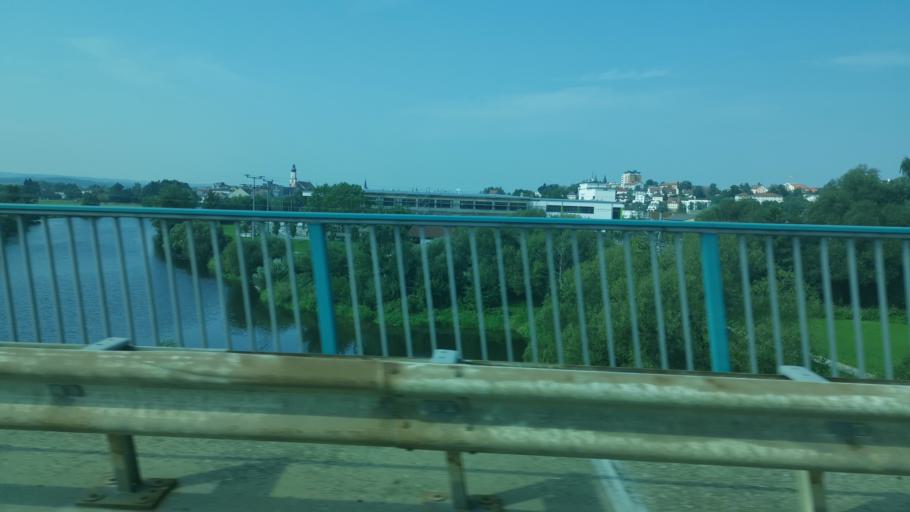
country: DE
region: Bavaria
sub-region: Upper Palatinate
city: Cham
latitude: 49.2226
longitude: 12.6787
